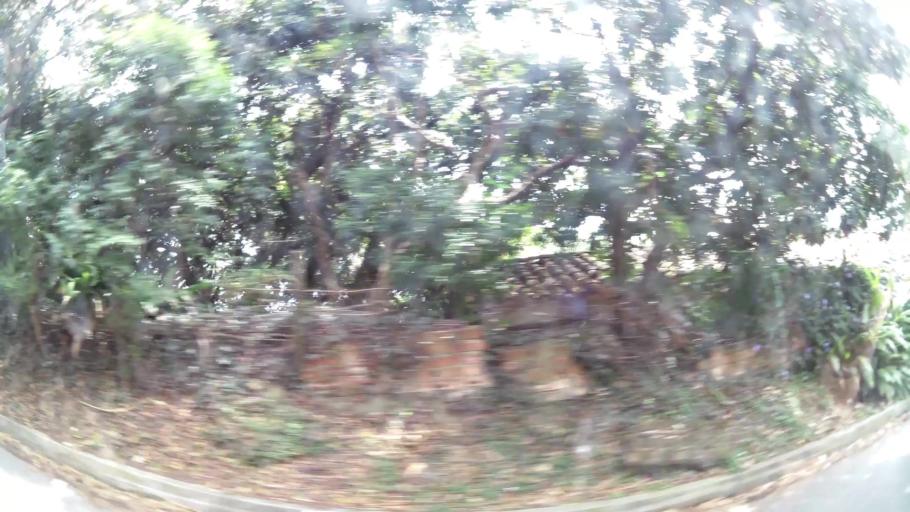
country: CO
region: Antioquia
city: Itagui
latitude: 6.1949
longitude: -75.5964
